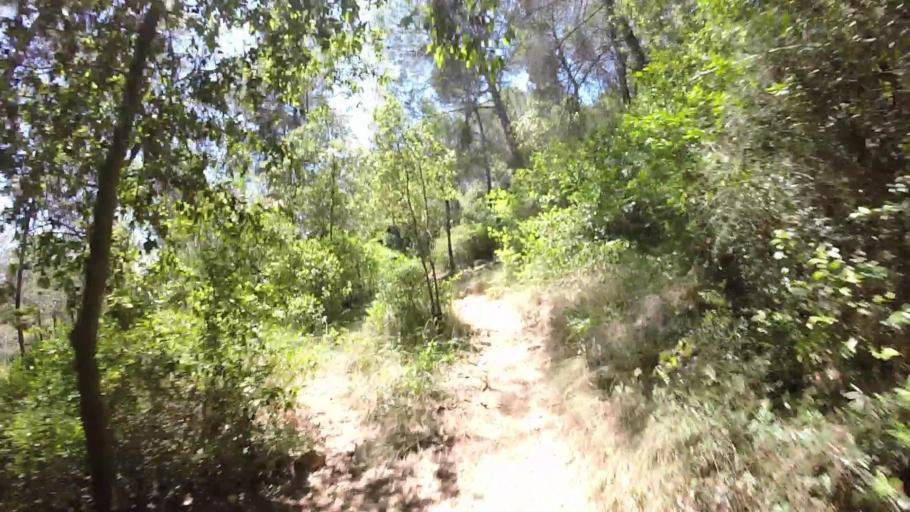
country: FR
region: Provence-Alpes-Cote d'Azur
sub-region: Departement des Alpes-Maritimes
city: Vallauris
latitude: 43.6123
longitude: 7.0472
